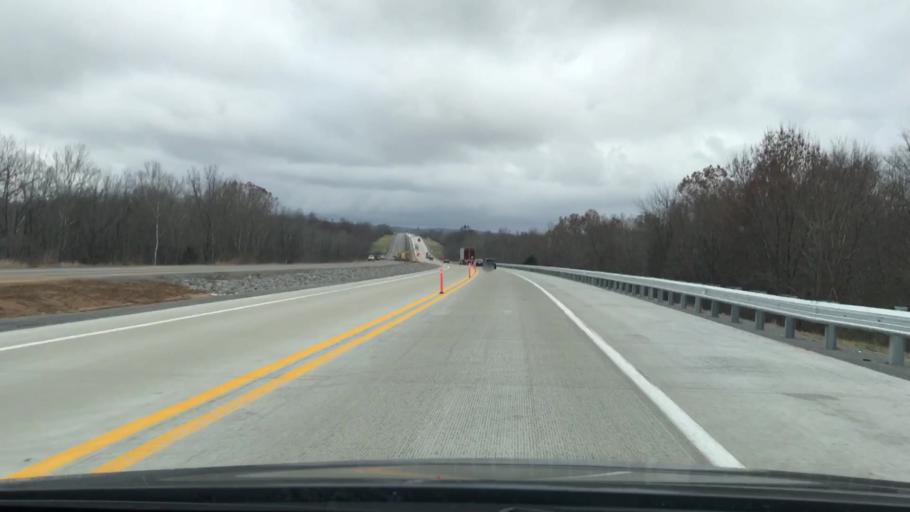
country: US
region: Kentucky
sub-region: Christian County
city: Hopkinsville
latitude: 37.0159
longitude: -87.4570
